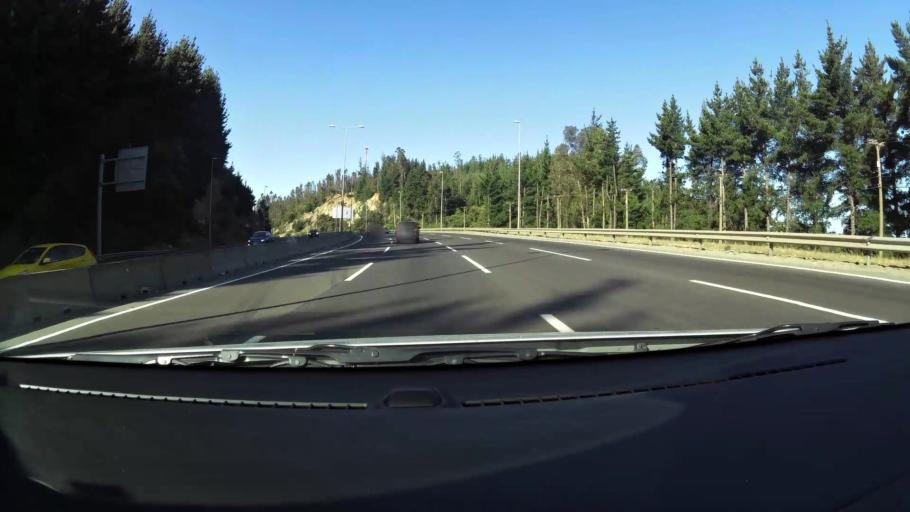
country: CL
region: Valparaiso
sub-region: Provincia de Valparaiso
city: Vina del Mar
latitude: -33.1064
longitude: -71.5493
